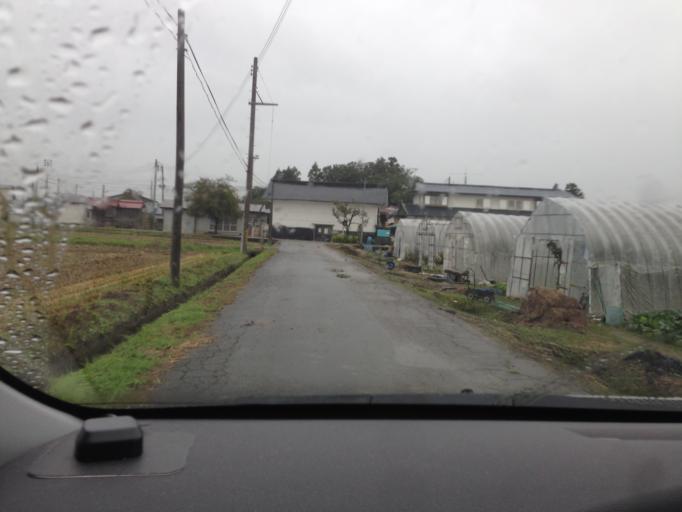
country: JP
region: Fukushima
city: Kitakata
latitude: 37.4592
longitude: 139.8731
